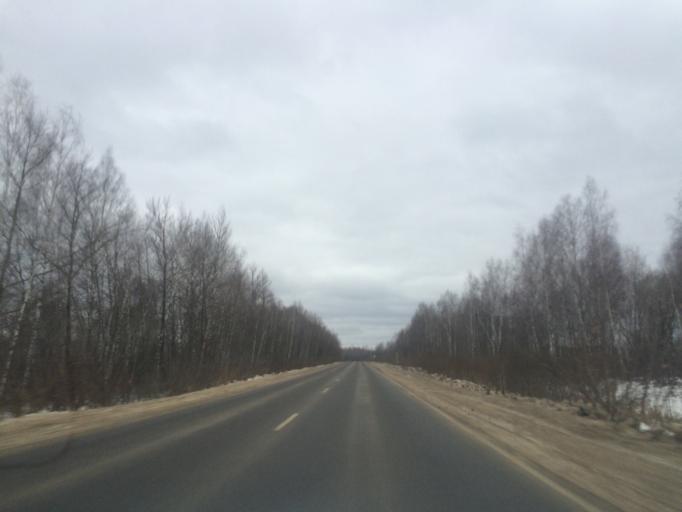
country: RU
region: Tula
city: Odoyev
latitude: 54.0043
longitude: 36.7657
